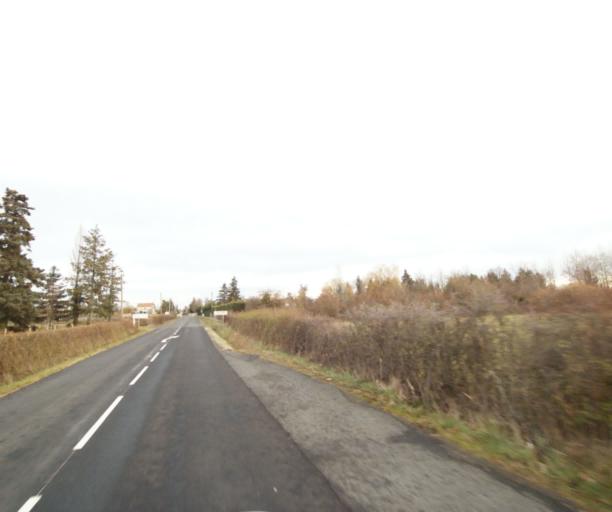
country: FR
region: Rhone-Alpes
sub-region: Departement de la Loire
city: Sury-le-Comtal
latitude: 45.5189
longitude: 4.1811
